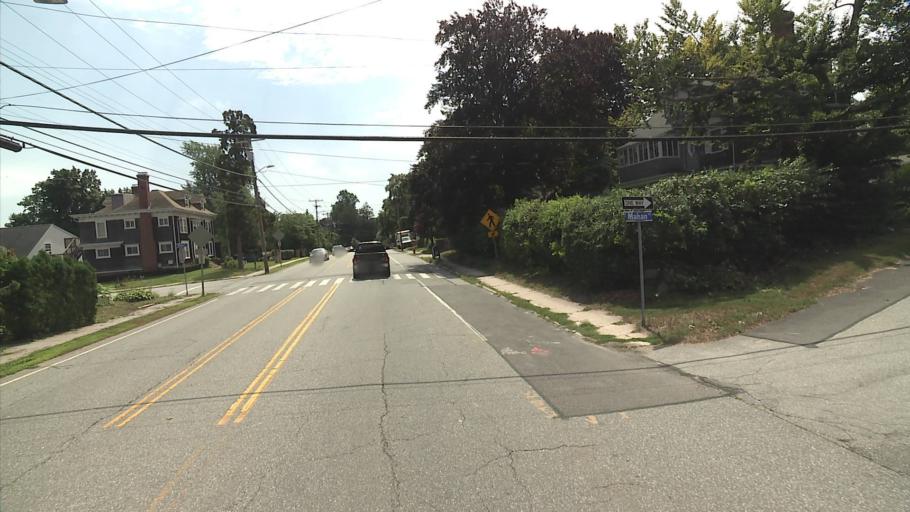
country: US
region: Connecticut
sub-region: New London County
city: New London
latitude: 41.3415
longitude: -72.1084
